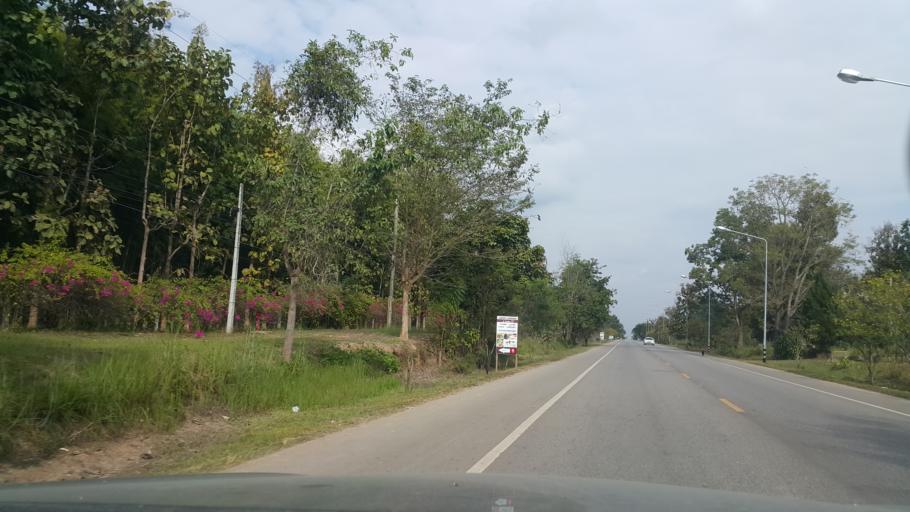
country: TH
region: Phayao
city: Phayao
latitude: 19.0885
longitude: 99.8996
